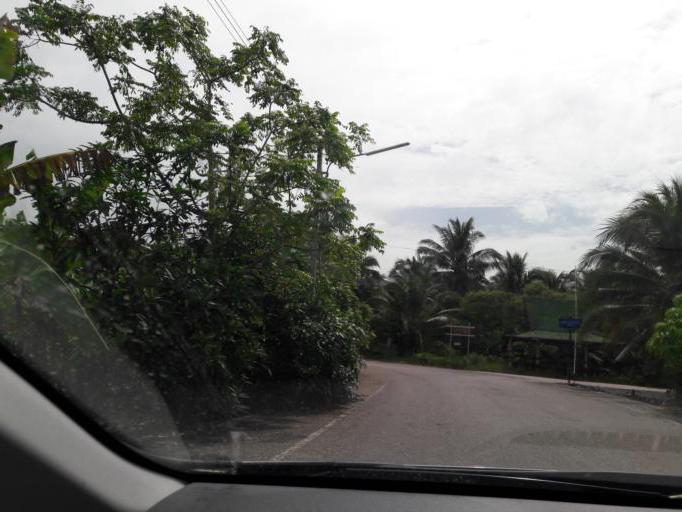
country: TH
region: Ratchaburi
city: Damnoen Saduak
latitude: 13.5217
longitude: 99.9987
